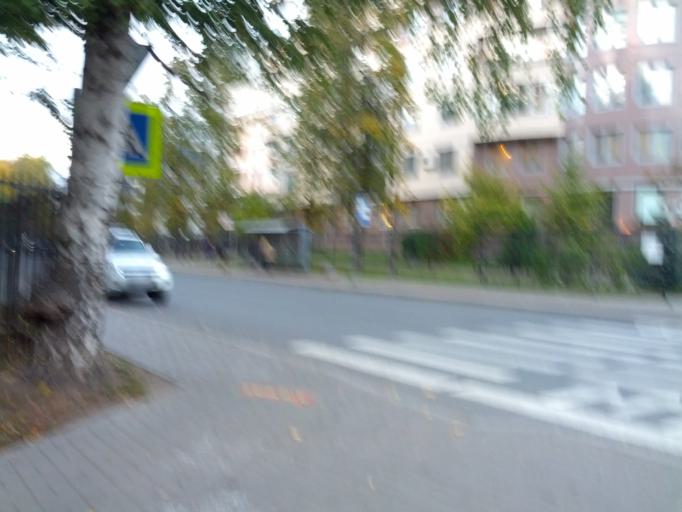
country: RU
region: Leningrad
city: Krestovskiy ostrov
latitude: 59.9692
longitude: 30.2590
